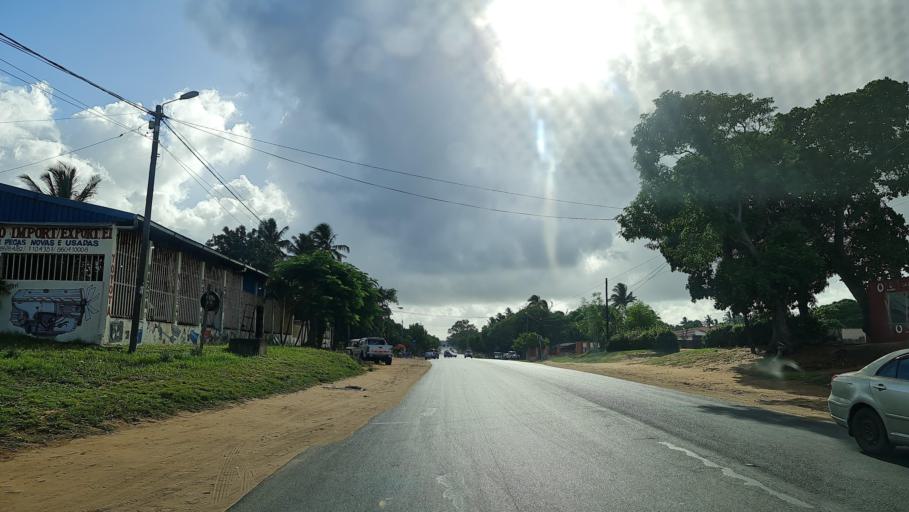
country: MZ
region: Gaza
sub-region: Xai-Xai District
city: Xai-Xai
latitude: -25.0568
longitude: 33.6832
